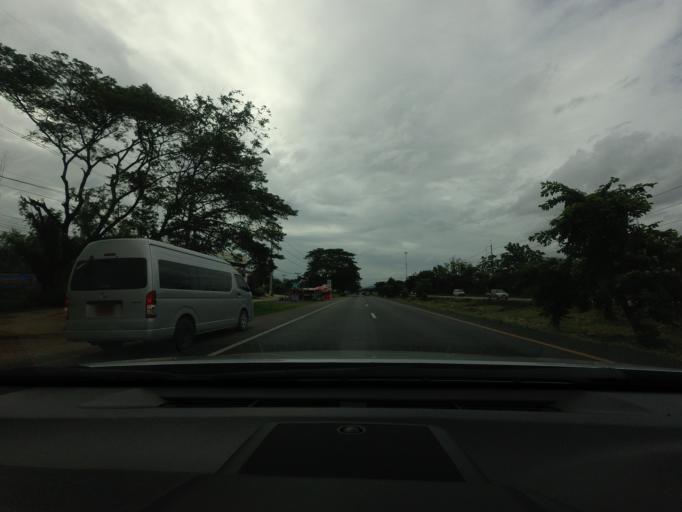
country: TH
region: Prachuap Khiri Khan
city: Hua Hin
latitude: 12.5920
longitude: 99.8639
